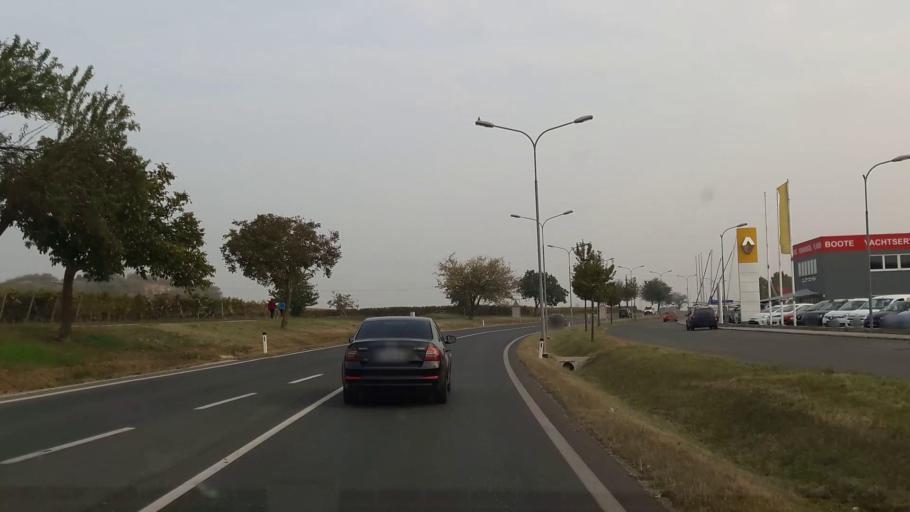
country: AT
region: Burgenland
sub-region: Politischer Bezirk Neusiedl am See
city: Weiden am See
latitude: 47.9214
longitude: 16.8766
